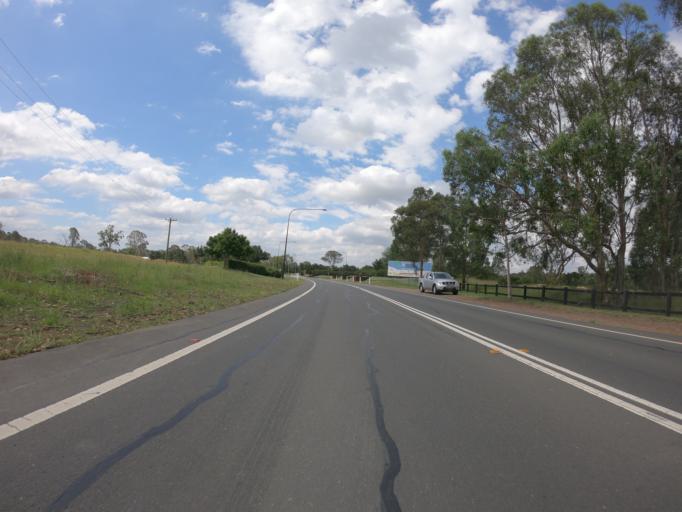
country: AU
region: New South Wales
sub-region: Penrith Municipality
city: Kingswood Park
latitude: -33.8336
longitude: 150.7564
